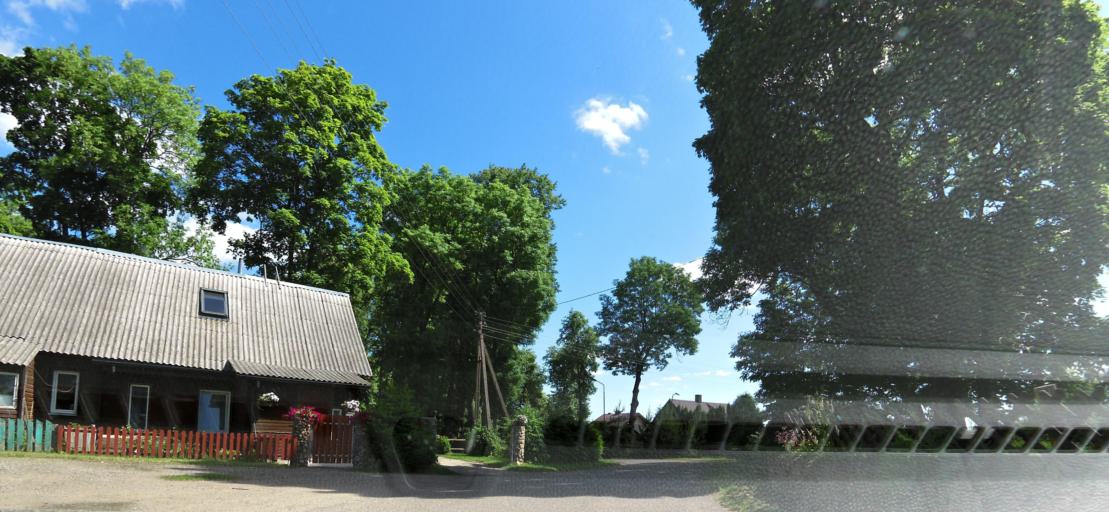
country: LT
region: Vilnius County
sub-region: Vilnius
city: Fabijoniskes
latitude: 54.8268
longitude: 25.2819
